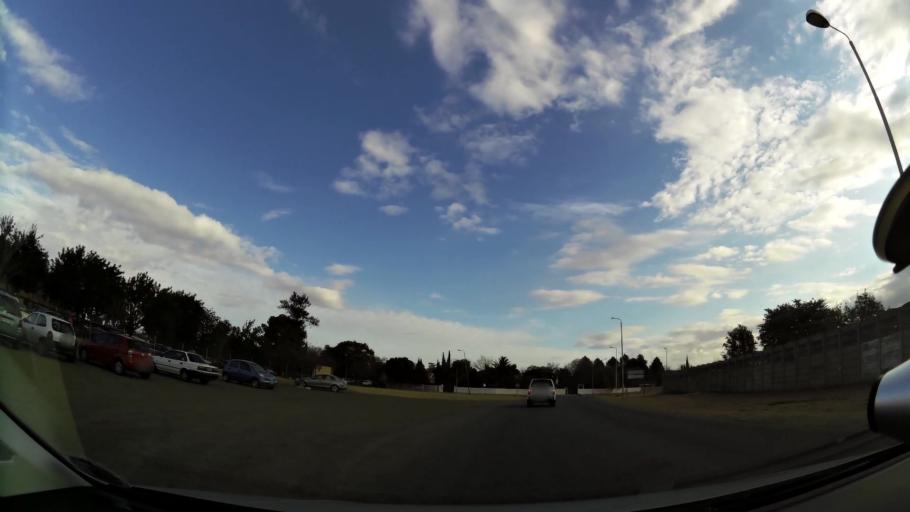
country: ZA
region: Orange Free State
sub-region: Lejweleputswa District Municipality
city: Welkom
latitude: -27.9880
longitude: 26.7294
